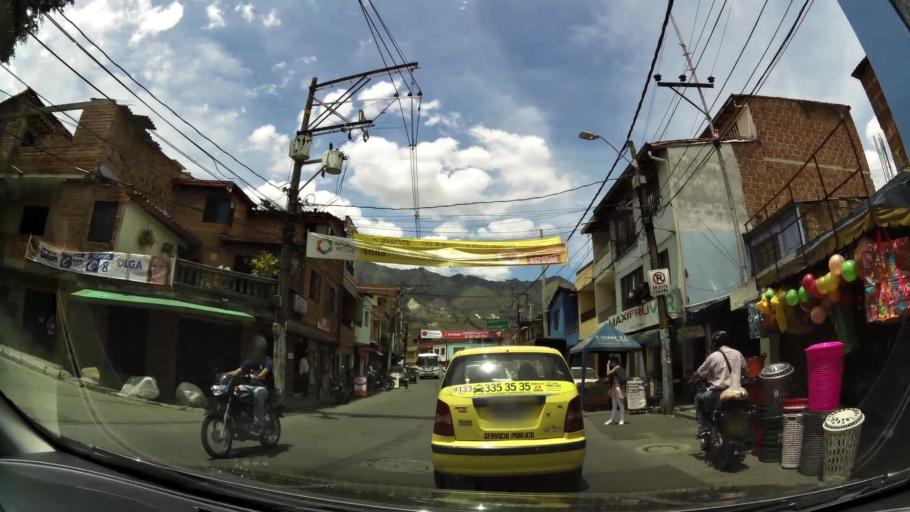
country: CO
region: Antioquia
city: Bello
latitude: 6.3437
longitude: -75.5635
